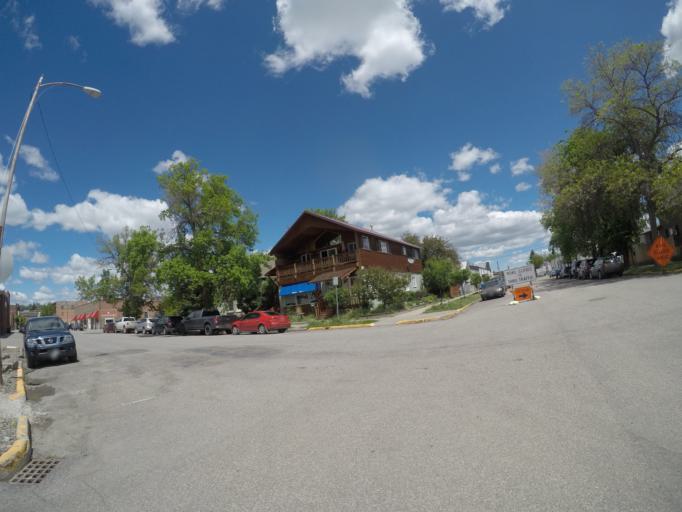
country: US
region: Montana
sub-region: Park County
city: Livingston
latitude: 45.6588
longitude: -110.5591
